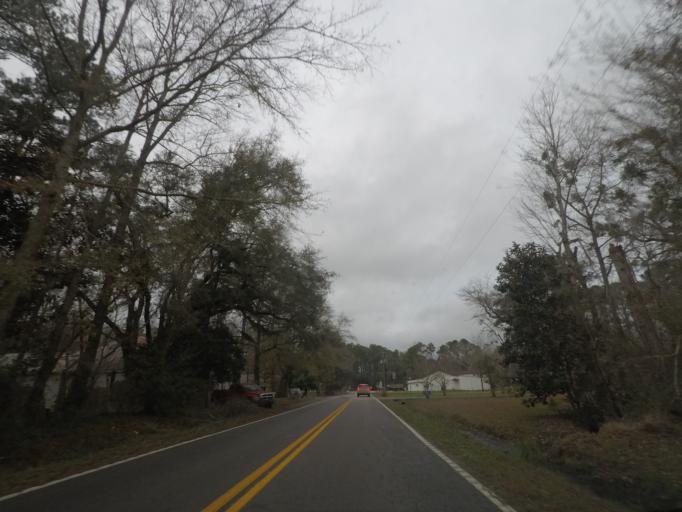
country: US
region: South Carolina
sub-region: Colleton County
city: Walterboro
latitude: 32.9364
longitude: -80.5400
